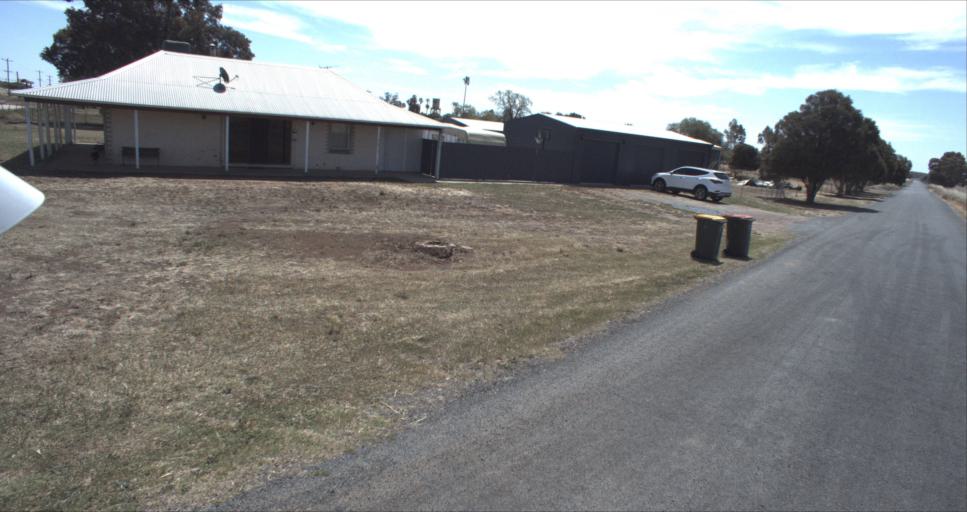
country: AU
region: New South Wales
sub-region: Leeton
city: Leeton
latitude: -34.6067
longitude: 146.4146
